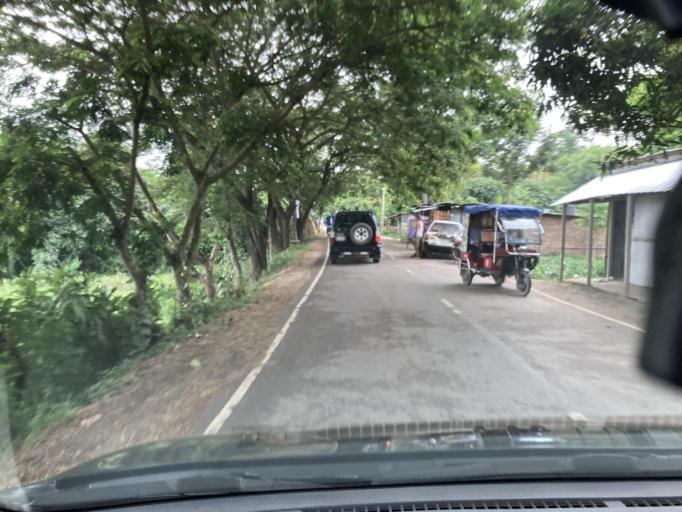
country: BD
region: Dhaka
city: Azimpur
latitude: 23.7723
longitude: 90.2047
